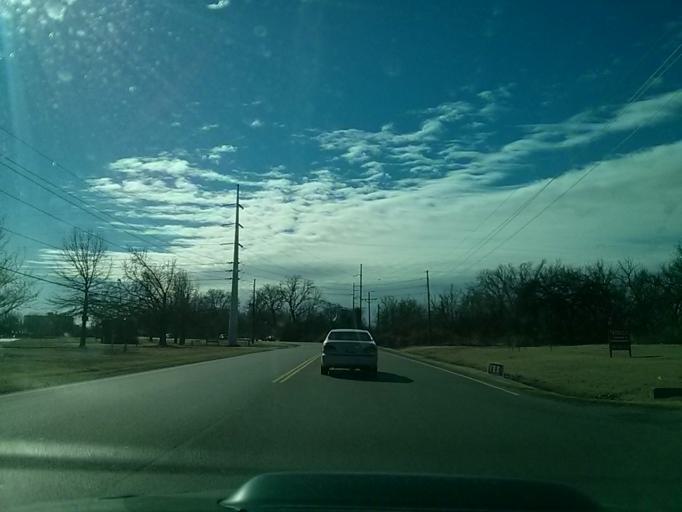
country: US
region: Oklahoma
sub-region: Tulsa County
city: Jenks
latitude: 36.0427
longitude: -95.9579
